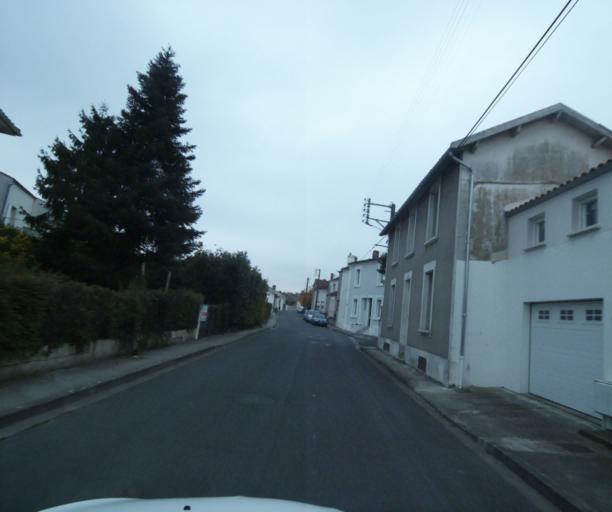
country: FR
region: Poitou-Charentes
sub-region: Departement de la Charente-Maritime
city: Saintes
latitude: 45.7450
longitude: -0.6138
